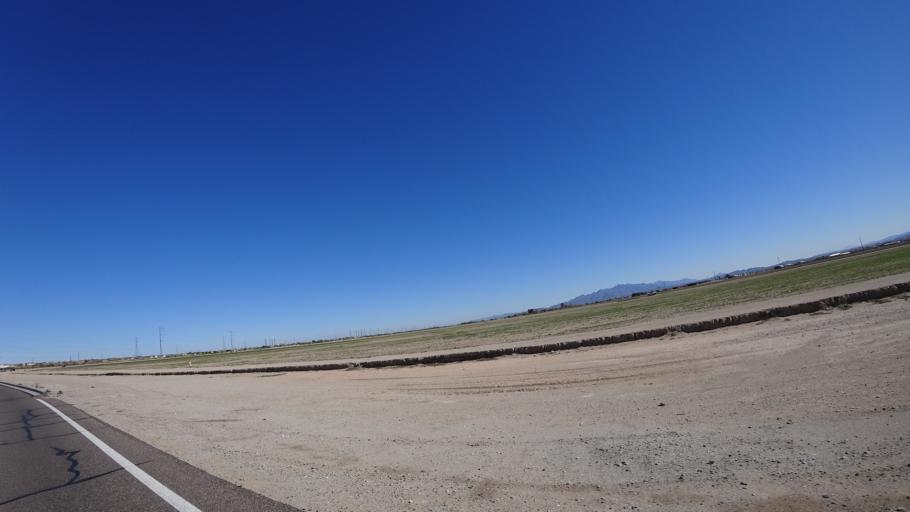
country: US
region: Arizona
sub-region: Maricopa County
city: Buckeye
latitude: 33.4188
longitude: -112.5698
